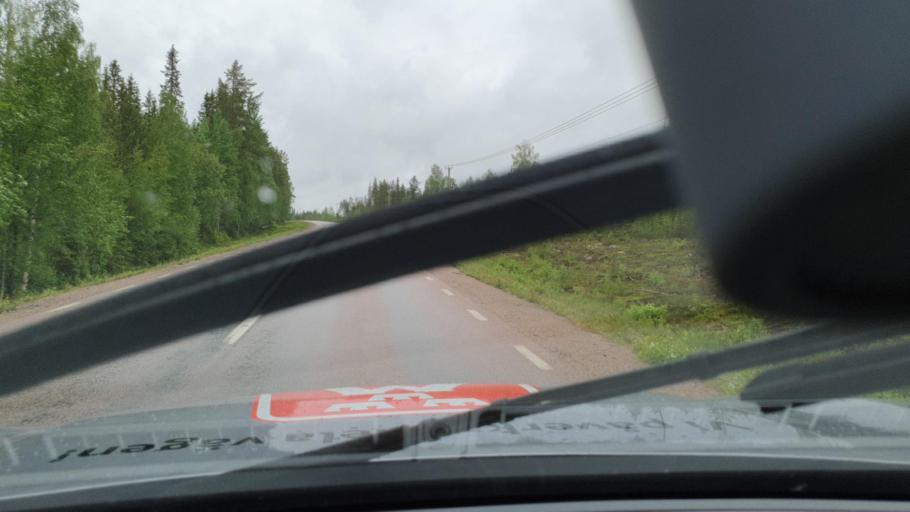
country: SE
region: Norrbotten
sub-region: Overkalix Kommun
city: OEverkalix
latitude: 66.4178
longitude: 22.9632
